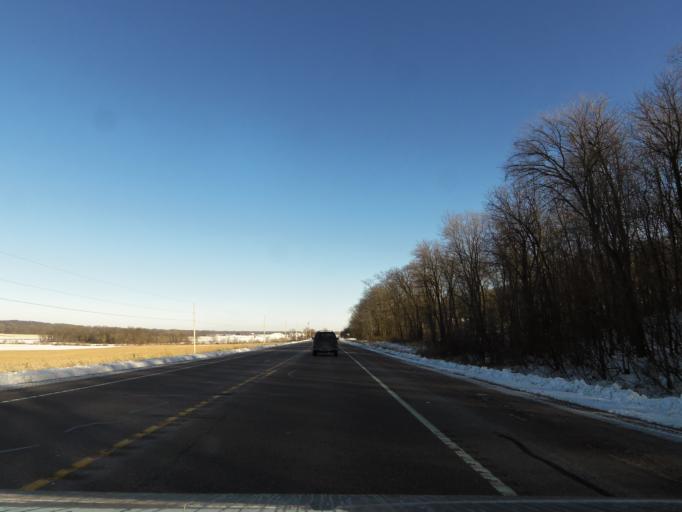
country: US
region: Wisconsin
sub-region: Columbia County
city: Lake Wisconsin
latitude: 43.5049
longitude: -89.6044
